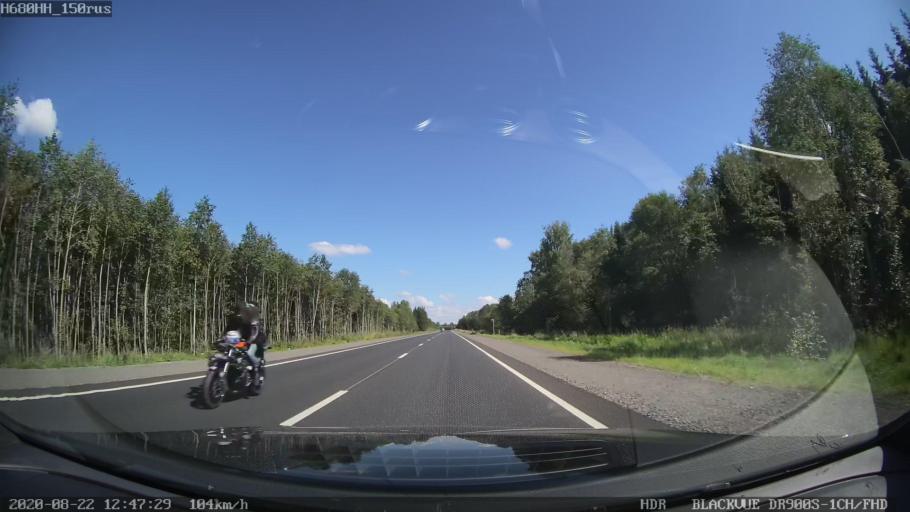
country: RU
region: Tverskaya
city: Rameshki
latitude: 57.4299
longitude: 36.1673
